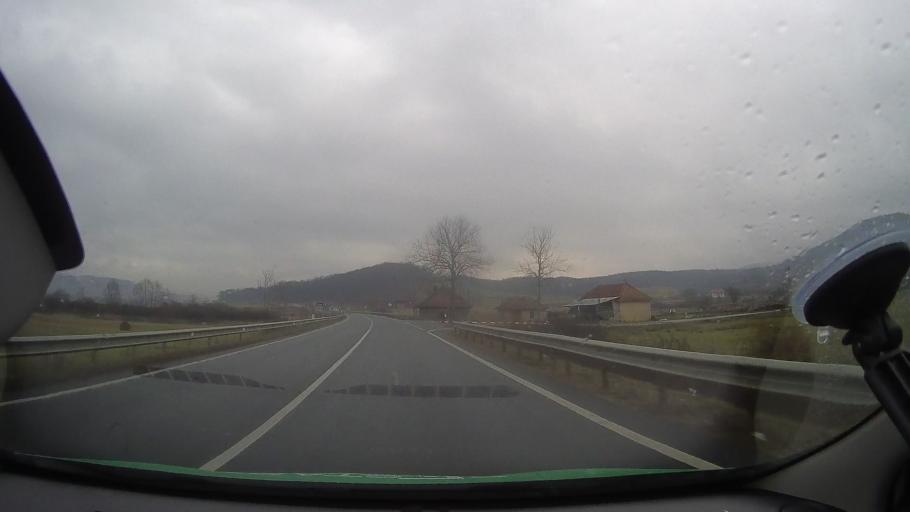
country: RO
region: Hunedoara
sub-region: Comuna Baia de Cris
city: Baia de Cris
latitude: 46.1780
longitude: 22.6863
